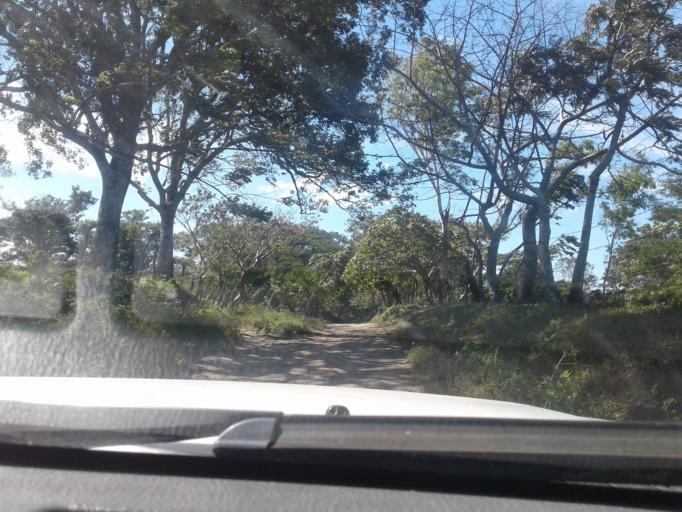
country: NI
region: Carazo
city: Santa Teresa
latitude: 11.7829
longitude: -86.1860
